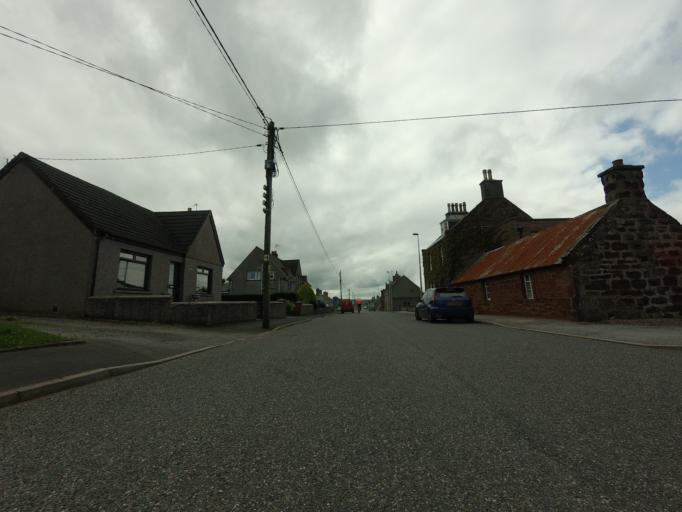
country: GB
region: Scotland
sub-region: Aberdeenshire
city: Turriff
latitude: 57.5431
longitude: -2.3261
